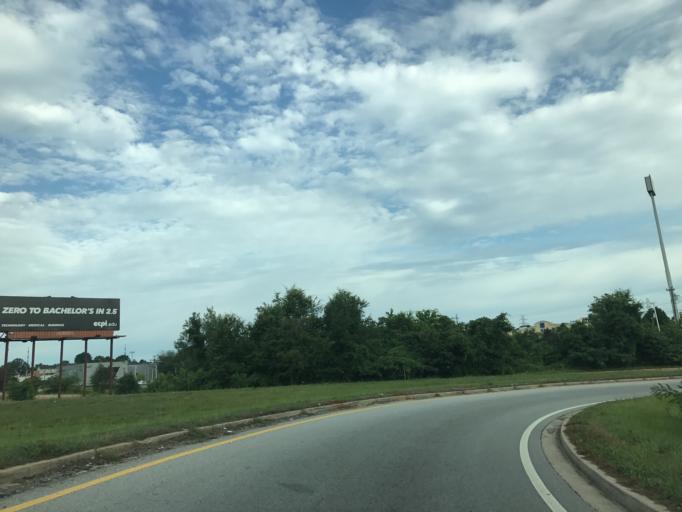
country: US
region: South Carolina
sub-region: Greenville County
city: Mauldin
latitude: 34.8136
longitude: -82.3377
